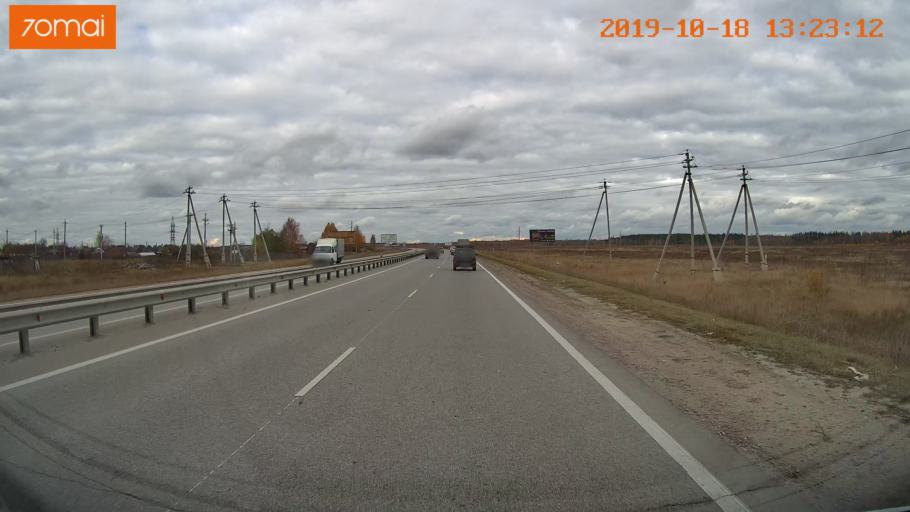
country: RU
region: Rjazan
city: Polyany
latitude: 54.7132
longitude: 39.8486
